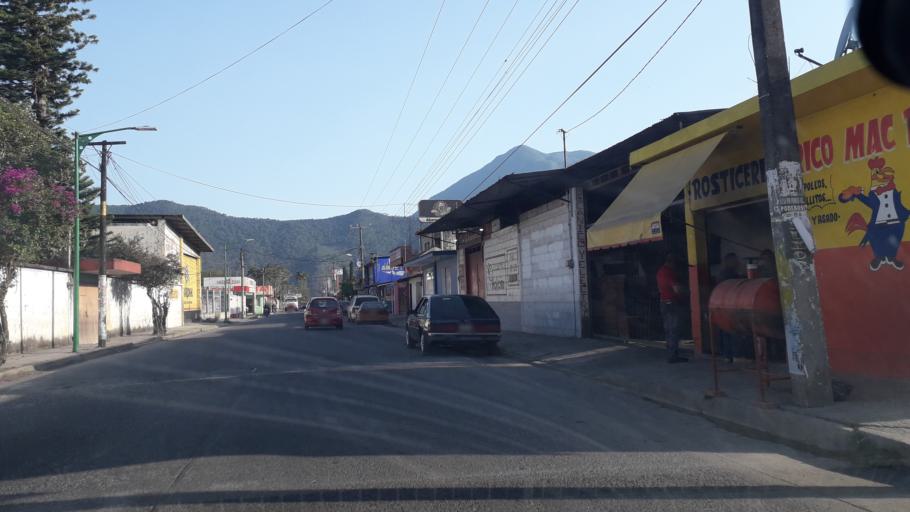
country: MX
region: Veracruz
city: Jalapilla
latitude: 18.8273
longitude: -97.0902
